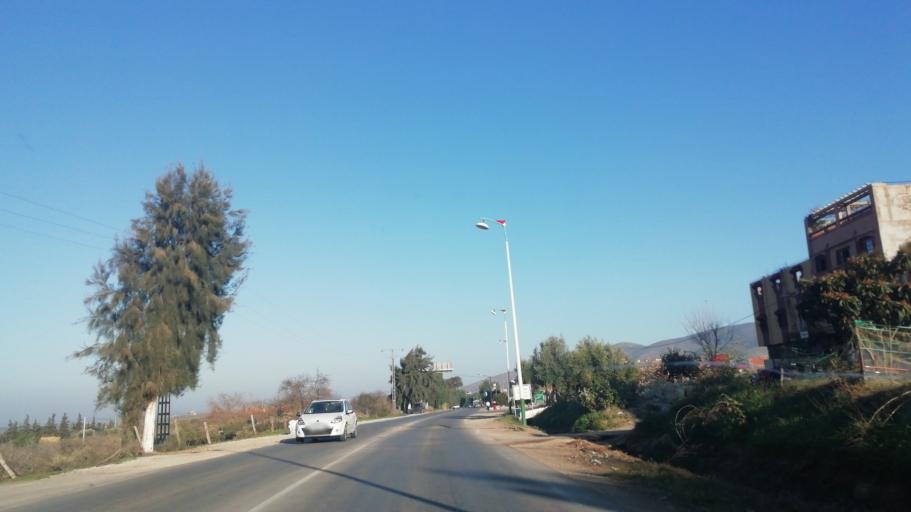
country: MA
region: Oriental
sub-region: Berkane-Taourirt
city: Ahfir
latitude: 34.9701
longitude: -2.1009
